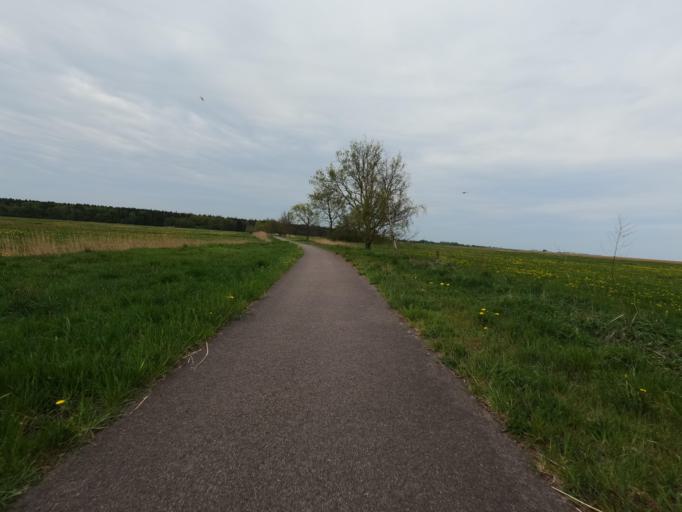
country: DE
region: Mecklenburg-Vorpommern
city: Born
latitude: 54.3563
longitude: 12.5593
